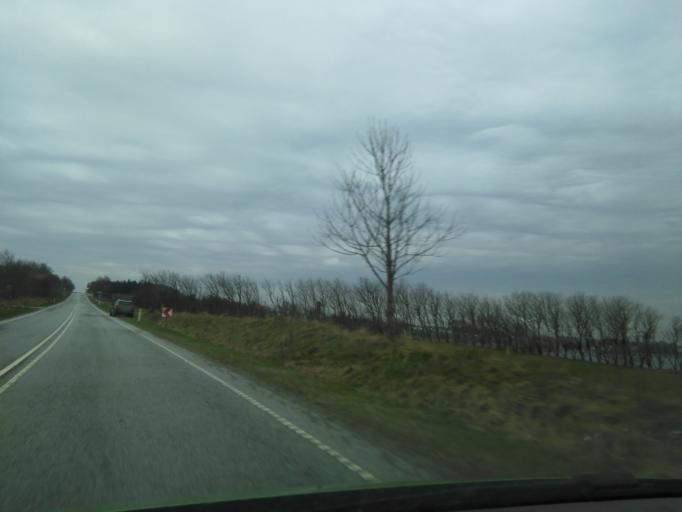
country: DK
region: North Denmark
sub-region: Mariagerfjord Kommune
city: Hadsund
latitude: 56.6845
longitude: 10.0935
